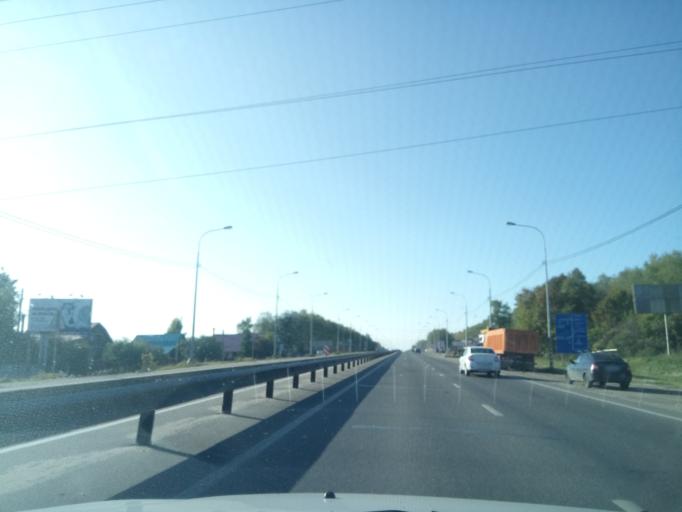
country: RU
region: Nizjnij Novgorod
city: Nizhniy Novgorod
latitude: 56.2142
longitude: 43.9297
